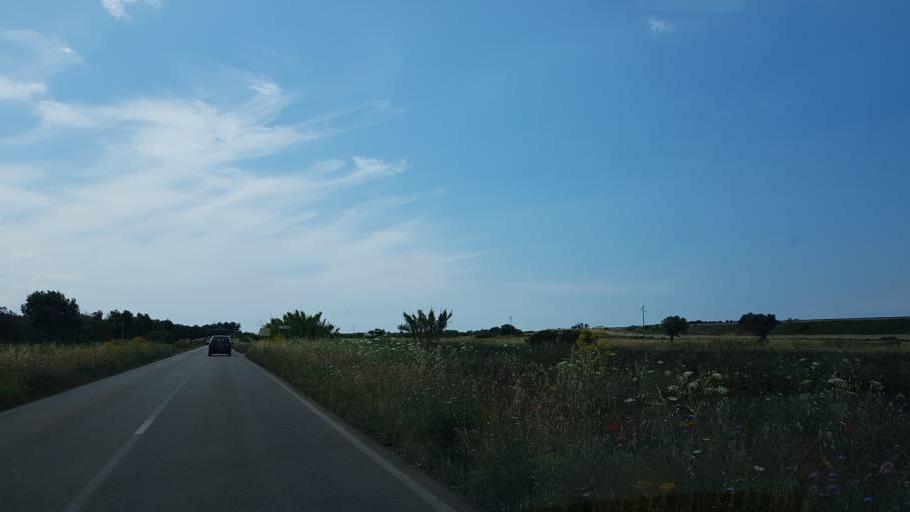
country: IT
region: Apulia
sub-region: Provincia di Lecce
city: Porto Cesareo
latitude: 40.3326
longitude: 17.8516
